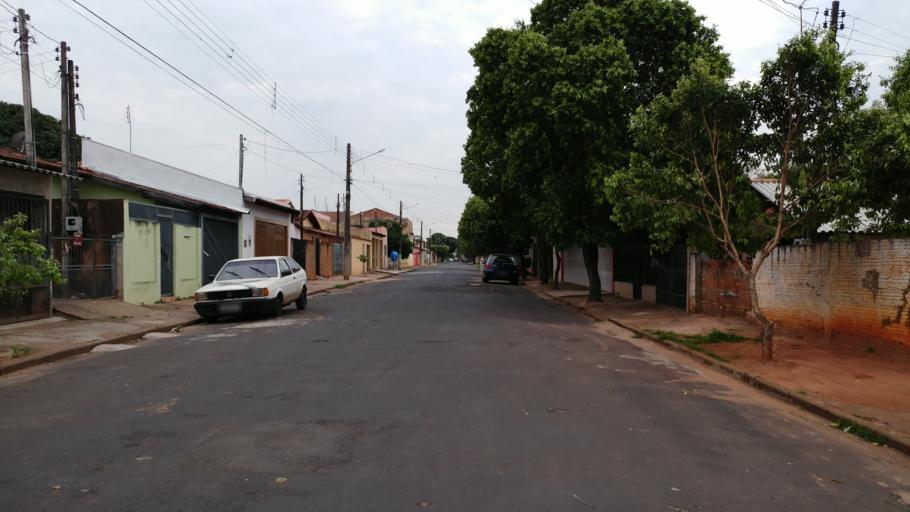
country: BR
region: Sao Paulo
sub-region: Paraguacu Paulista
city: Paraguacu Paulista
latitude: -22.4174
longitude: -50.5710
